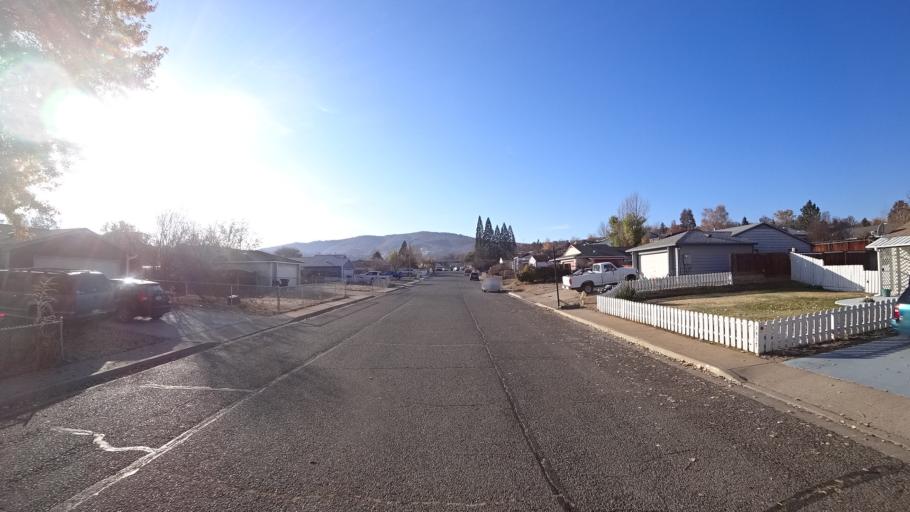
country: US
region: California
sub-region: Siskiyou County
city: Yreka
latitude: 41.7099
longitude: -122.6205
